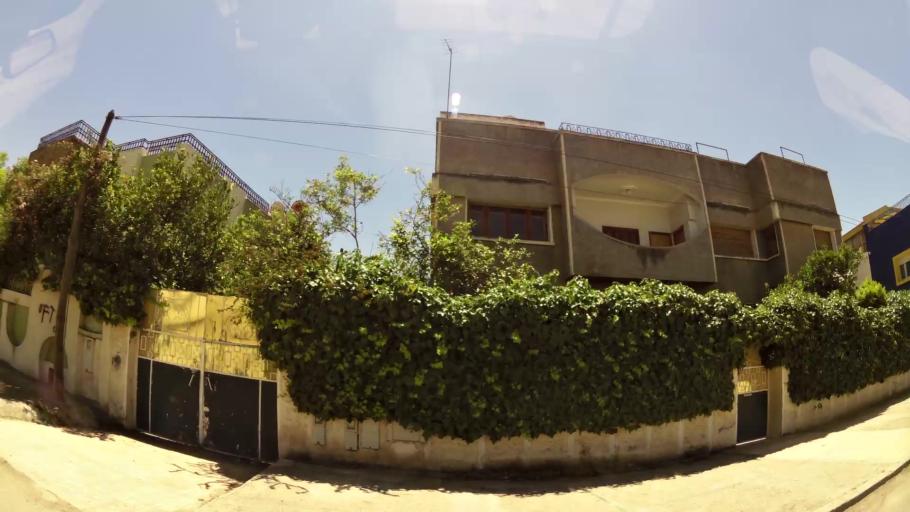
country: MA
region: Fes-Boulemane
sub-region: Fes
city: Fes
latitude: 34.0276
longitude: -5.0069
